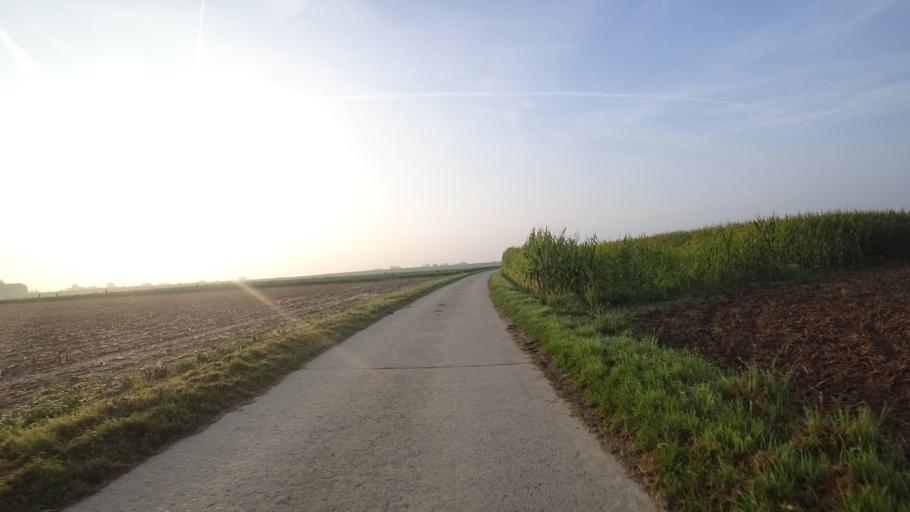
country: BE
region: Wallonia
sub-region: Province du Brabant Wallon
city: Walhain-Saint-Paul
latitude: 50.6420
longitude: 4.6921
